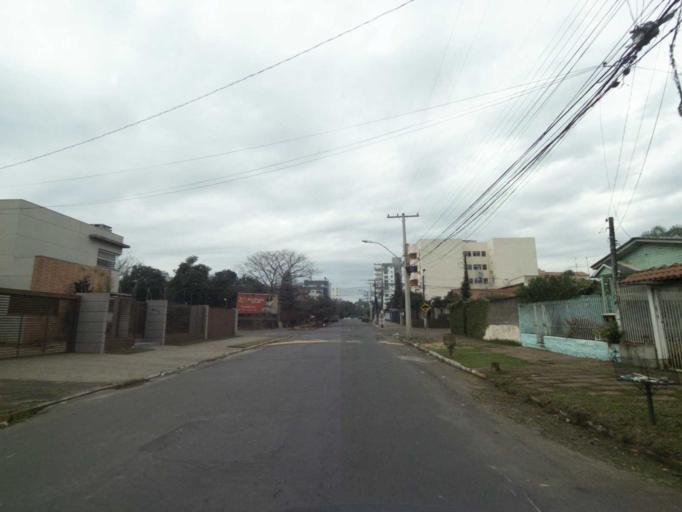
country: BR
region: Rio Grande do Sul
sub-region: Sao Leopoldo
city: Sao Leopoldo
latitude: -29.7733
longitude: -51.1524
